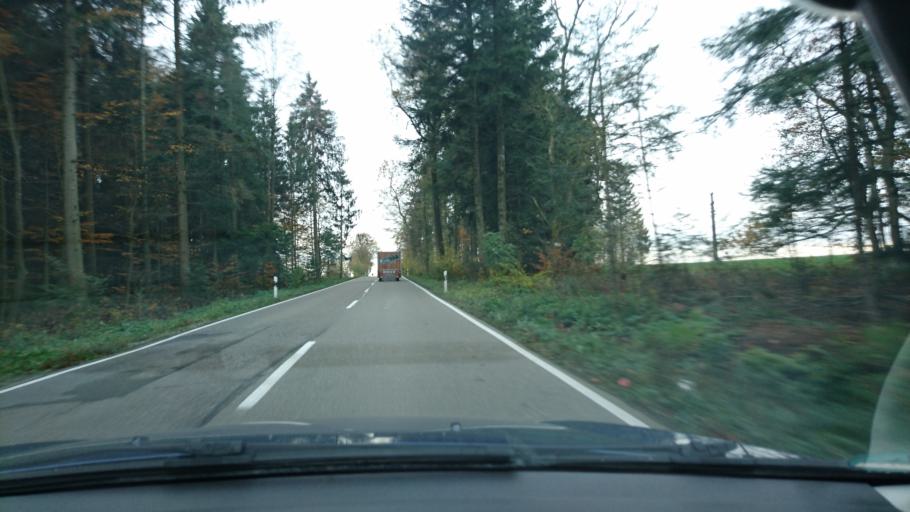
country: DE
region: Baden-Wuerttemberg
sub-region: Regierungsbezirk Stuttgart
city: Welzheim
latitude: 48.8964
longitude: 9.6604
